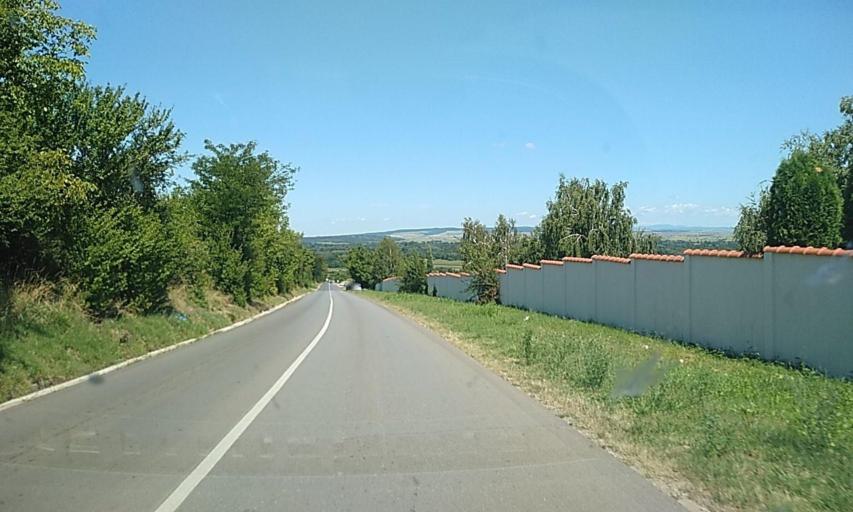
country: RS
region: Central Serbia
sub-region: Branicevski Okrug
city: Pozarevac
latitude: 44.6394
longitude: 21.2055
